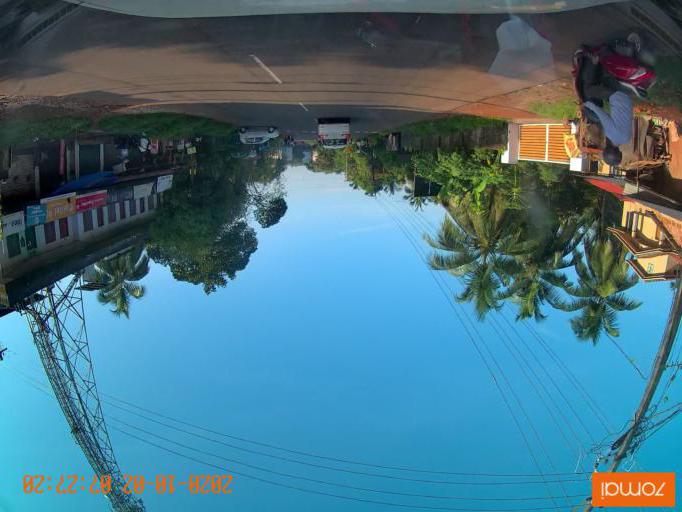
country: IN
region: Kerala
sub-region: Malappuram
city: Pariyapuram
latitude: 11.0230
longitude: 75.9477
